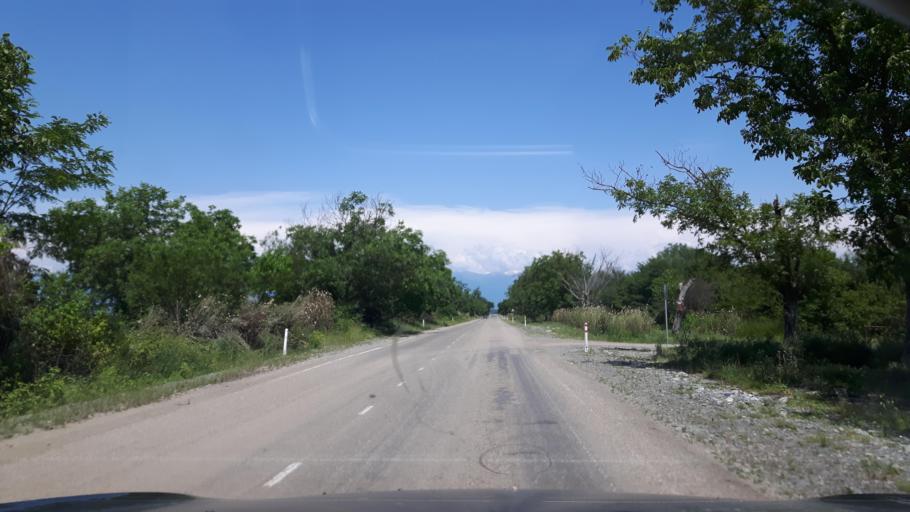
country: GE
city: Tsnori
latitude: 41.6354
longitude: 46.0292
